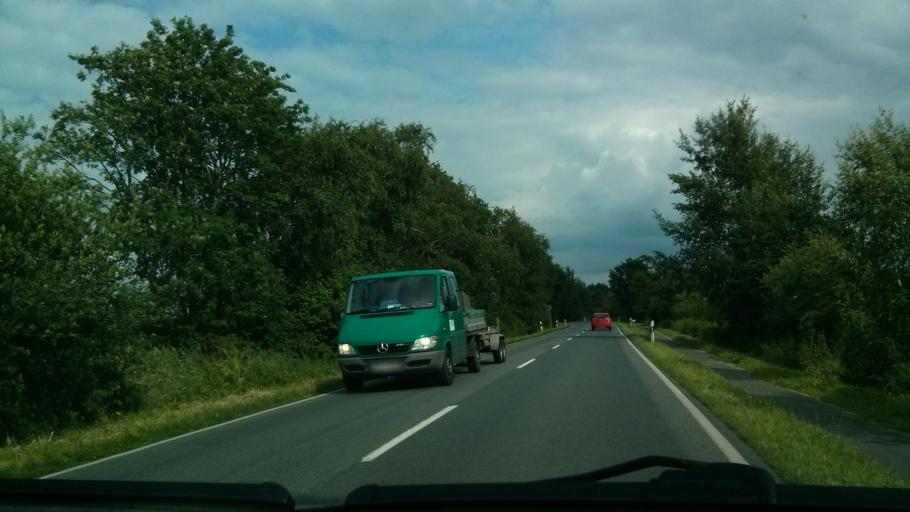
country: DE
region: Lower Saxony
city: Kuhrstedt
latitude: 53.5109
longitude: 8.7676
